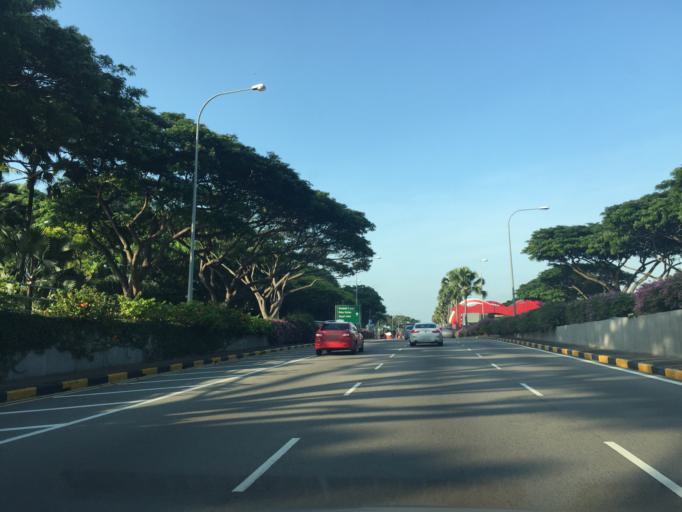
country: SG
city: Singapore
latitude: 1.3502
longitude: 103.9856
